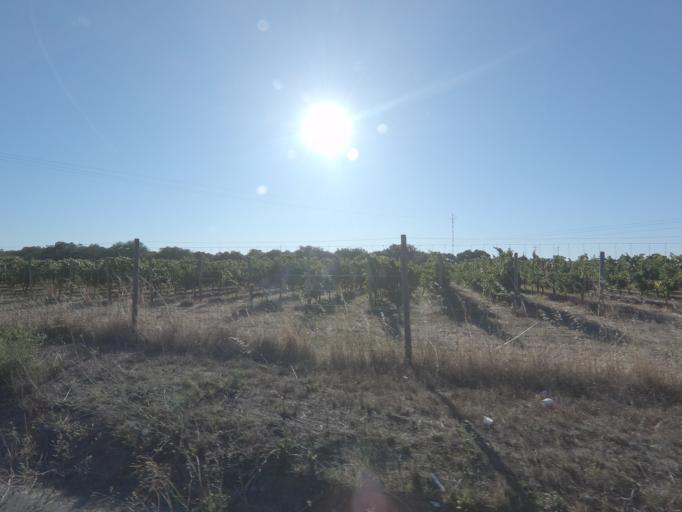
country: PT
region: Setubal
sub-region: Palmela
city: Quinta do Anjo
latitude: 38.5435
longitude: -8.9847
